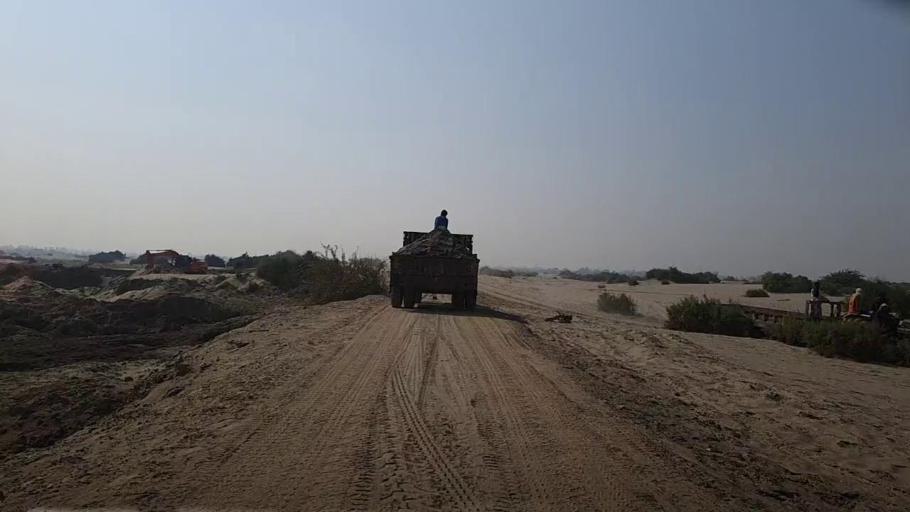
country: PK
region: Sindh
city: Bozdar
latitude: 27.2220
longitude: 68.5849
